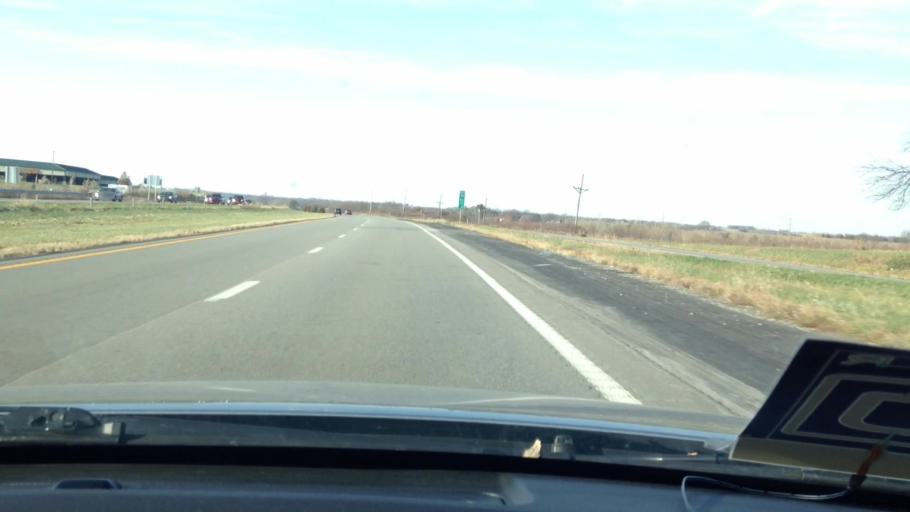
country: US
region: Missouri
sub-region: Platte County
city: Weatherby Lake
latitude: 39.3120
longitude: -94.6884
